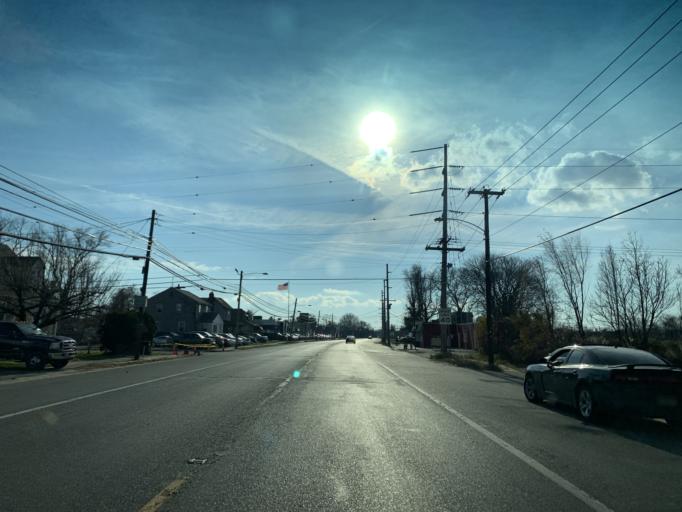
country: US
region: New Jersey
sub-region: Salem County
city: Penns Grove
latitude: 39.7315
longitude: -75.4606
